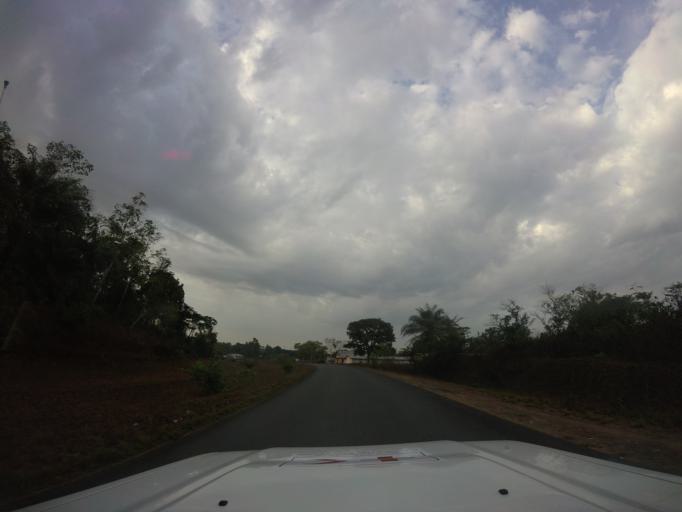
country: LR
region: Bomi
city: Tubmanburg
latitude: 6.7020
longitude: -10.8734
